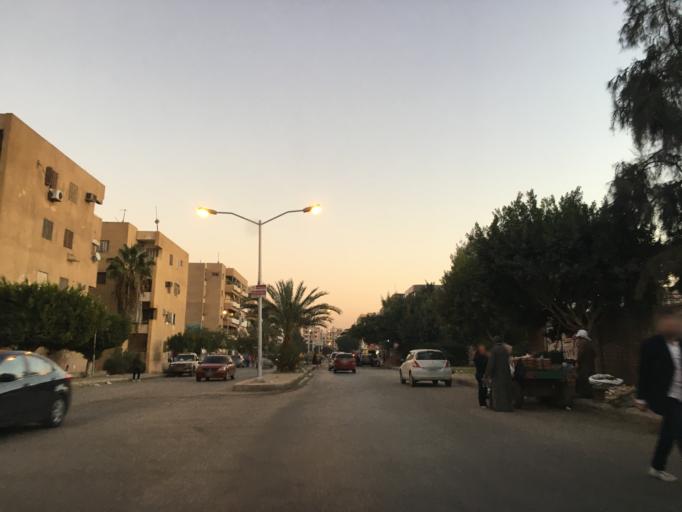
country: EG
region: Al Jizah
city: Madinat Sittah Uktubar
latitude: 29.9819
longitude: 30.9409
